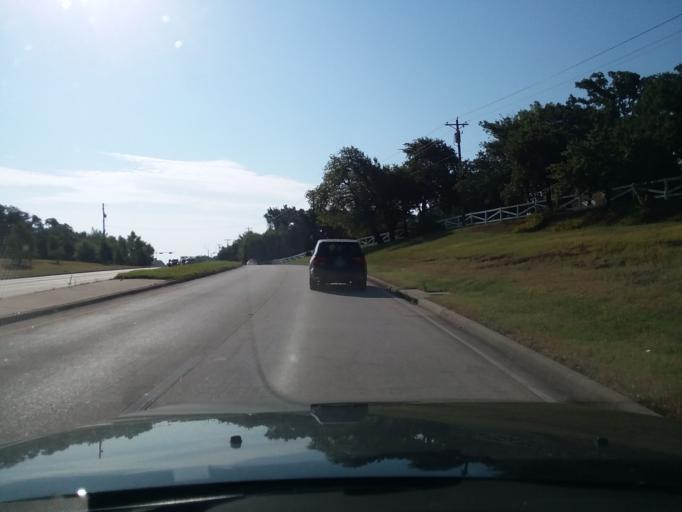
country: US
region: Texas
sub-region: Denton County
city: Bartonville
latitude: 33.0741
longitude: -97.1258
